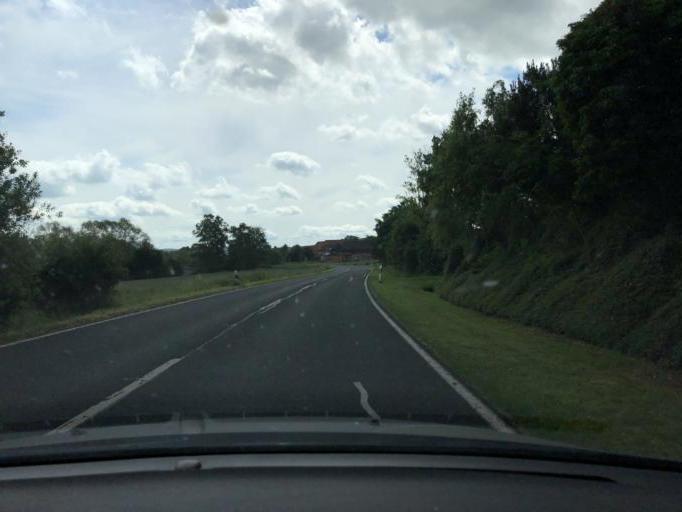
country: DE
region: Hesse
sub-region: Regierungsbezirk Kassel
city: Alheim
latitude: 51.0490
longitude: 9.6232
